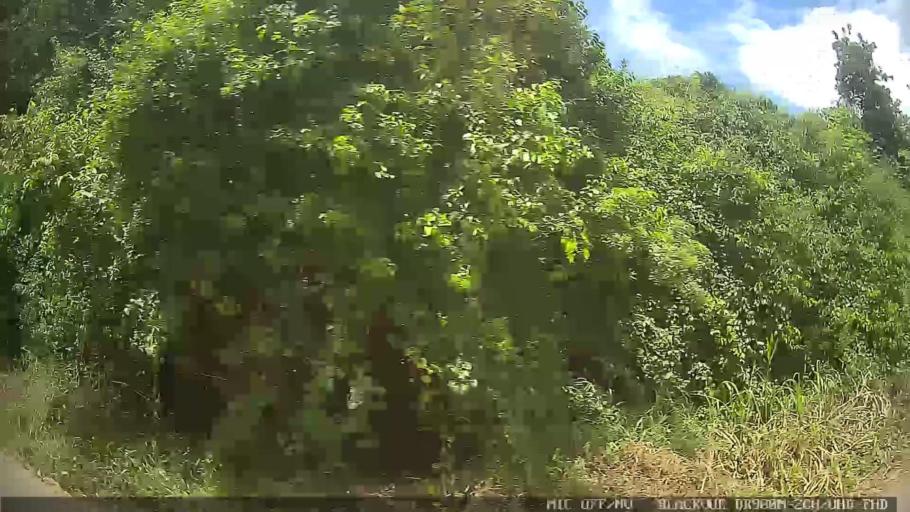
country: BR
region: Minas Gerais
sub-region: Extrema
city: Extrema
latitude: -22.8044
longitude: -46.4701
